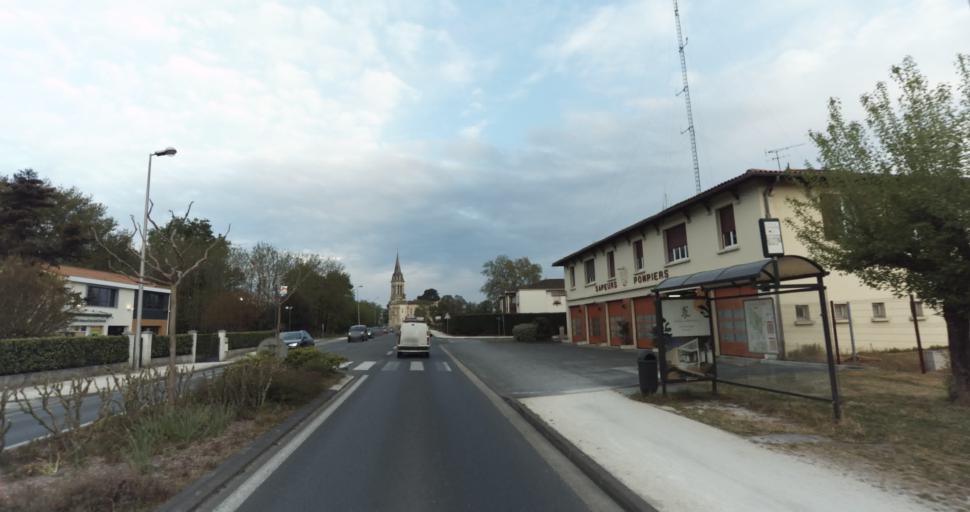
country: FR
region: Aquitaine
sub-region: Departement de la Gironde
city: Martignas-sur-Jalle
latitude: 44.8109
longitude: -0.7780
